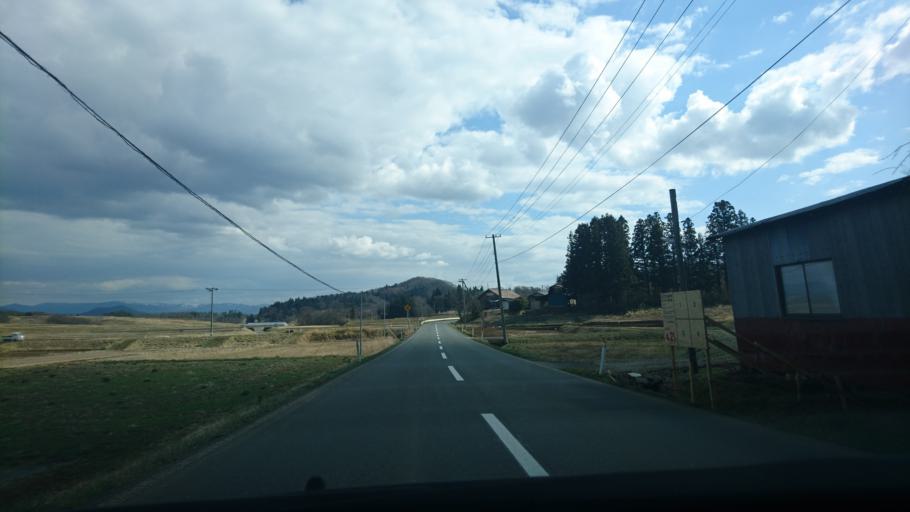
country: JP
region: Iwate
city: Kitakami
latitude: 39.2763
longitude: 141.2164
